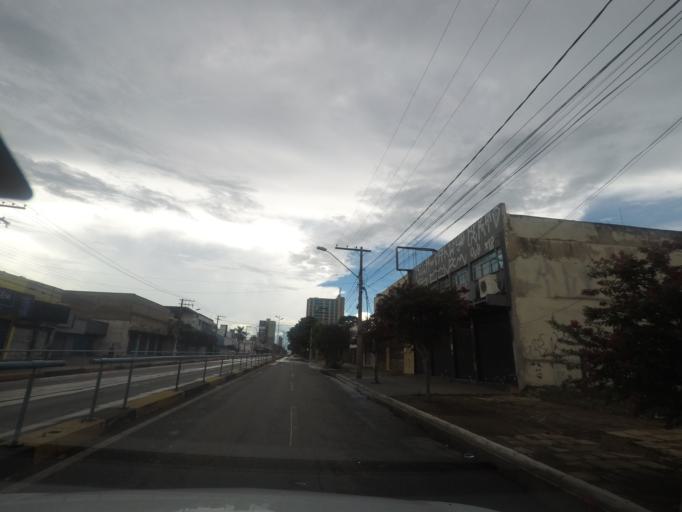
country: BR
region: Goias
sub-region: Goiania
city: Goiania
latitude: -16.6782
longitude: -49.2694
